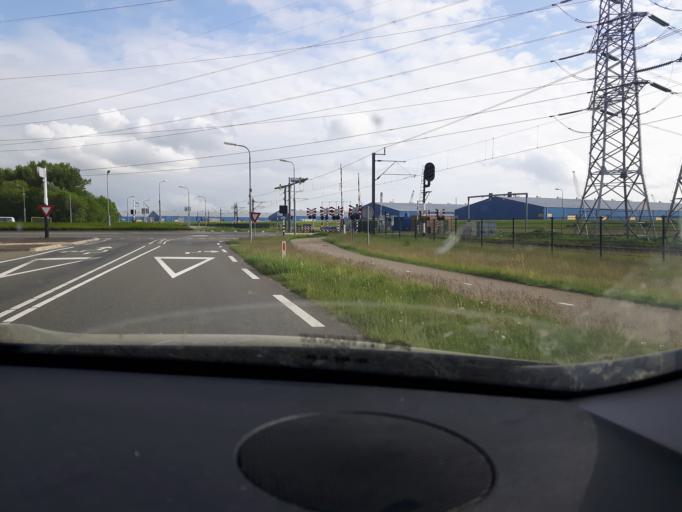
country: NL
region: Zeeland
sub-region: Gemeente Borsele
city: Borssele
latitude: 51.4636
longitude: 3.7284
